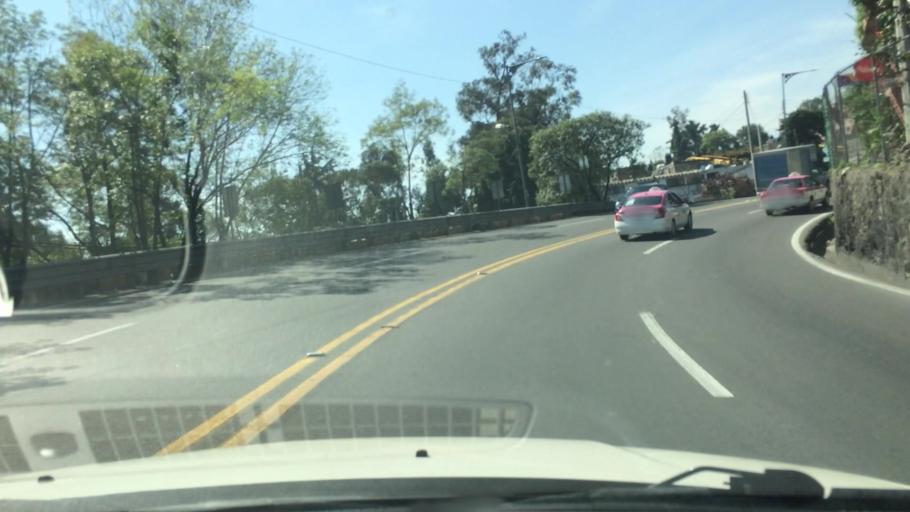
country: MX
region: Mexico City
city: Tlalpan
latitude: 19.2554
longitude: -99.1780
